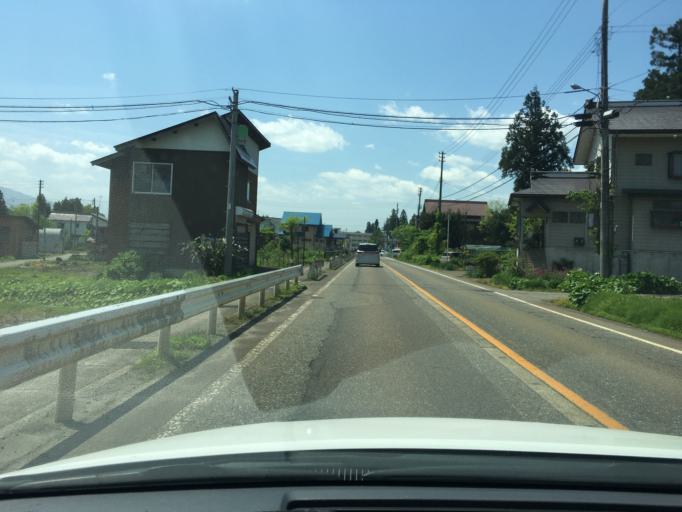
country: JP
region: Niigata
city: Ojiya
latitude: 37.2639
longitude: 138.9736
